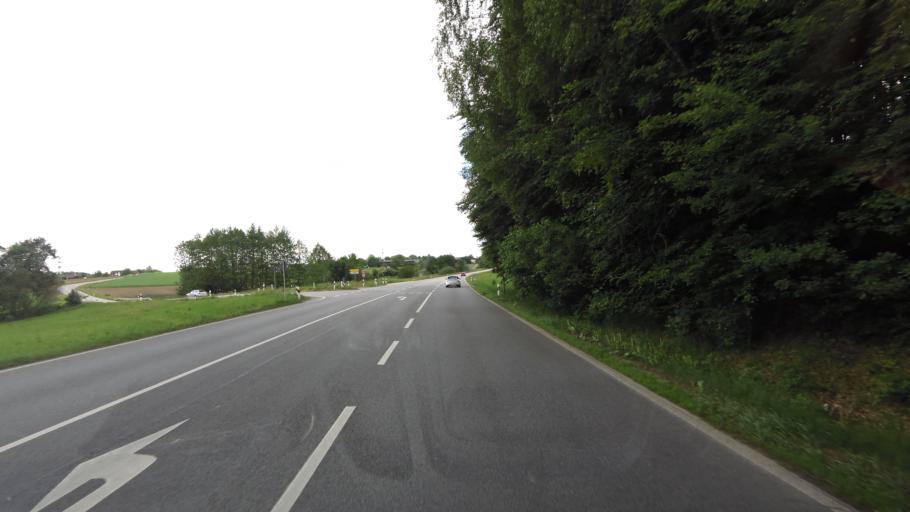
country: DE
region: Bavaria
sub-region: Upper Bavaria
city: Edling
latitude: 48.0459
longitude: 12.1849
